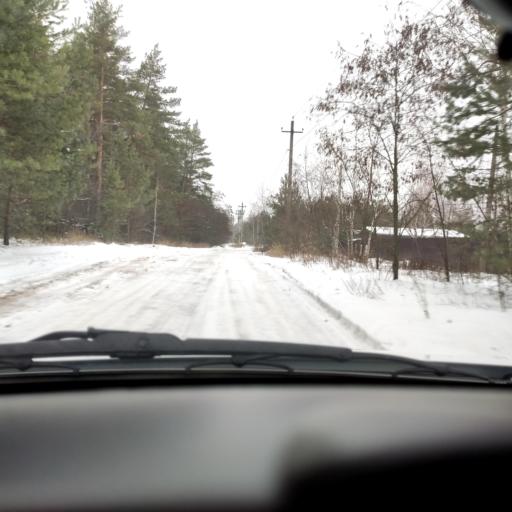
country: RU
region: Voronezj
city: Ramon'
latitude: 51.8847
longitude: 39.2585
